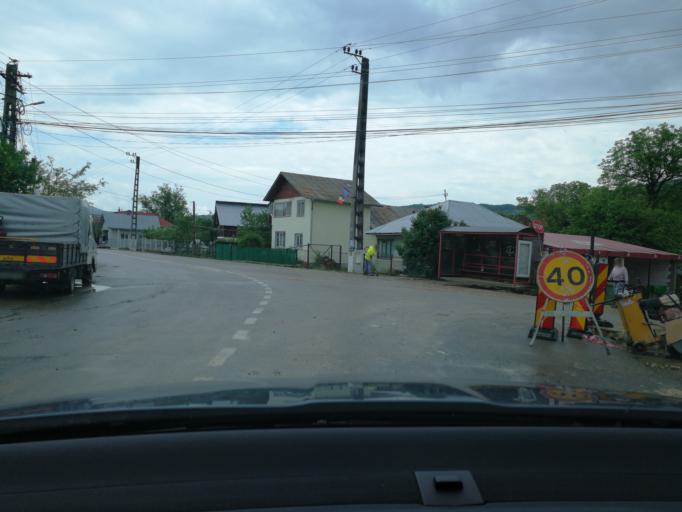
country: RO
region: Prahova
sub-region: Comuna Alunis
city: Ostrovu
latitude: 45.2002
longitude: 25.9006
